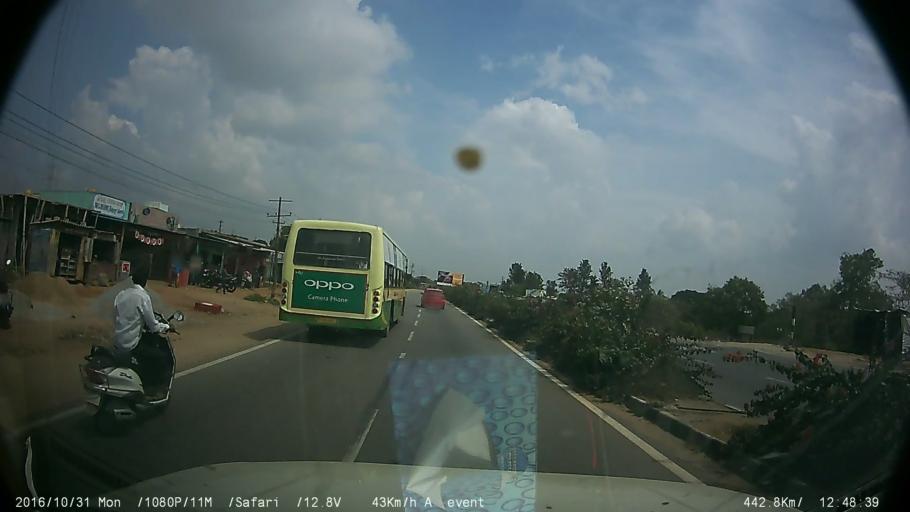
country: IN
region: Karnataka
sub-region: Mysore
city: Mysore
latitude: 12.3500
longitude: 76.5603
